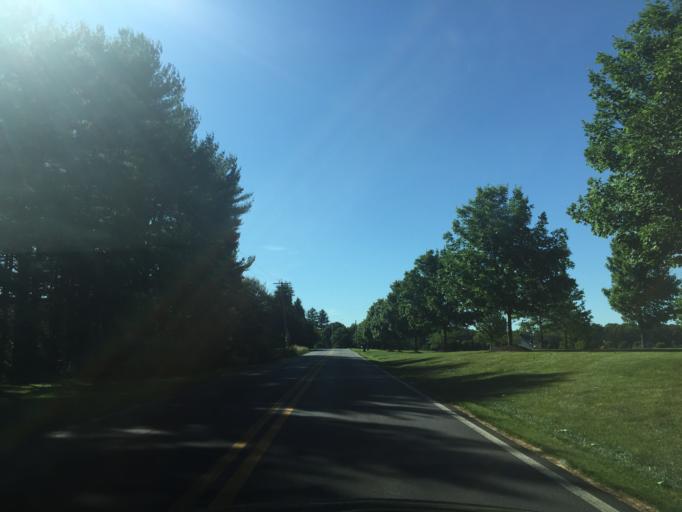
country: US
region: Maryland
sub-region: Carroll County
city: Westminster
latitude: 39.5805
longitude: -76.9259
